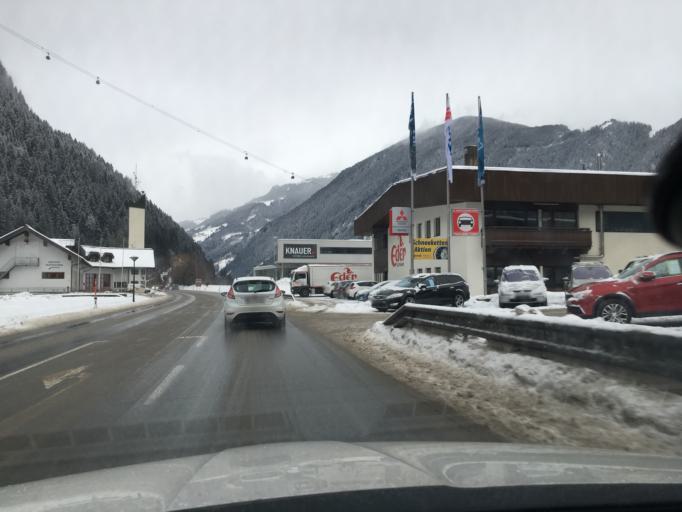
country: AT
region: Tyrol
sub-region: Politischer Bezirk Schwaz
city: Mayrhofen
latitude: 47.1609
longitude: 11.8504
